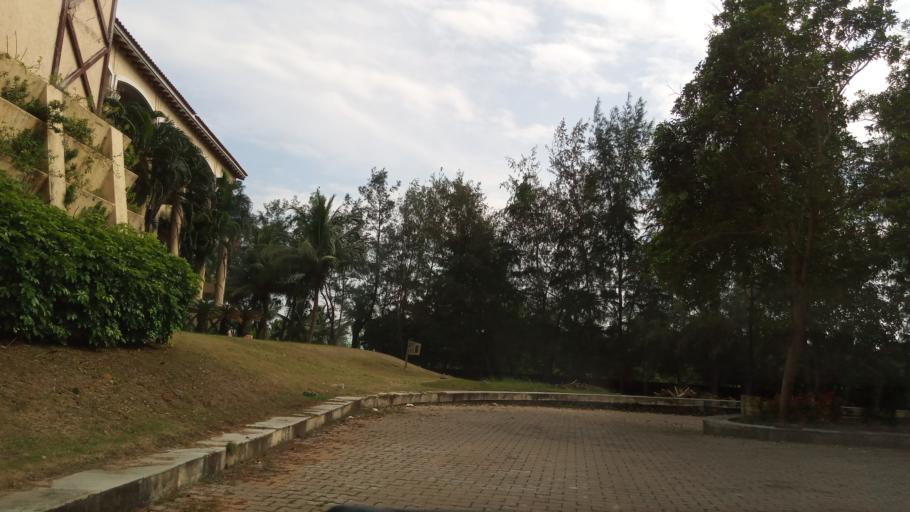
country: IN
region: Tamil Nadu
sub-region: Villupuram
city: Auroville
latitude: 12.0650
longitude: 79.8799
